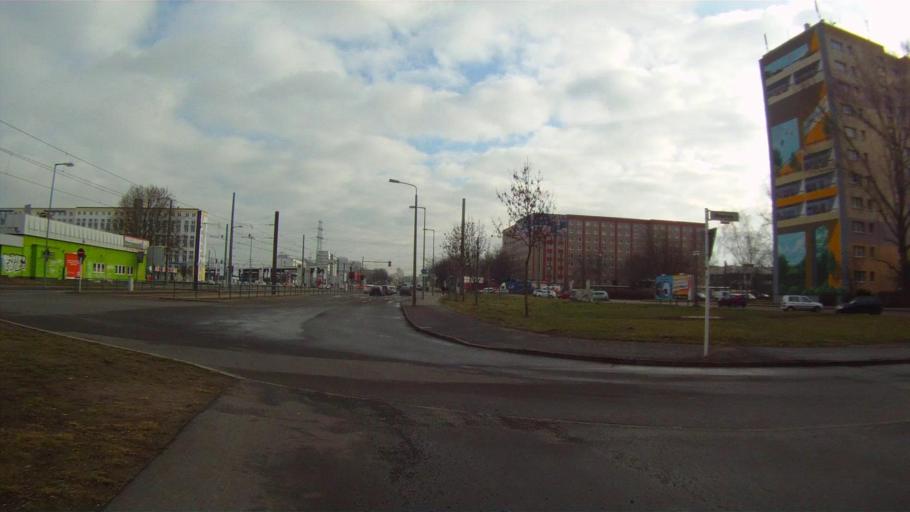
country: DE
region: Berlin
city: Lichtenberg
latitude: 52.5257
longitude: 13.5175
